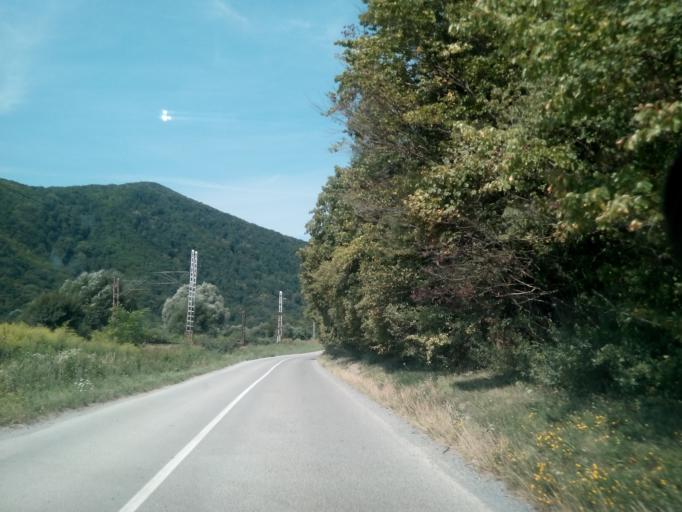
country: SK
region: Kosicky
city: Kosice
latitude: 48.8290
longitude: 21.2222
